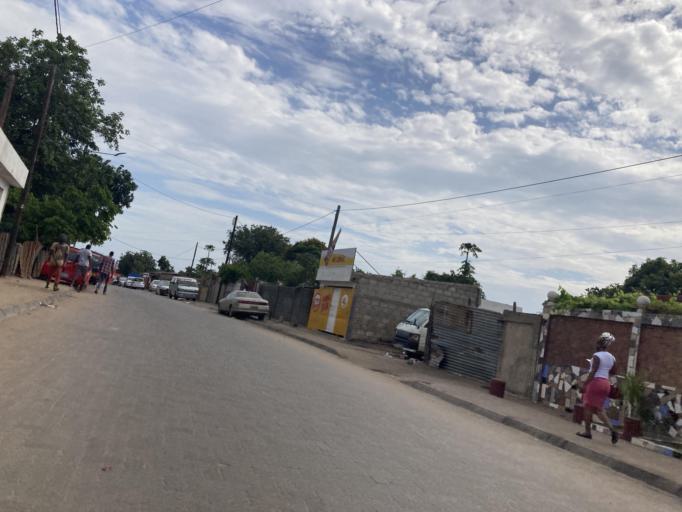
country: MZ
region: Maputo City
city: Maputo
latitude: -25.9337
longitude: 32.5856
